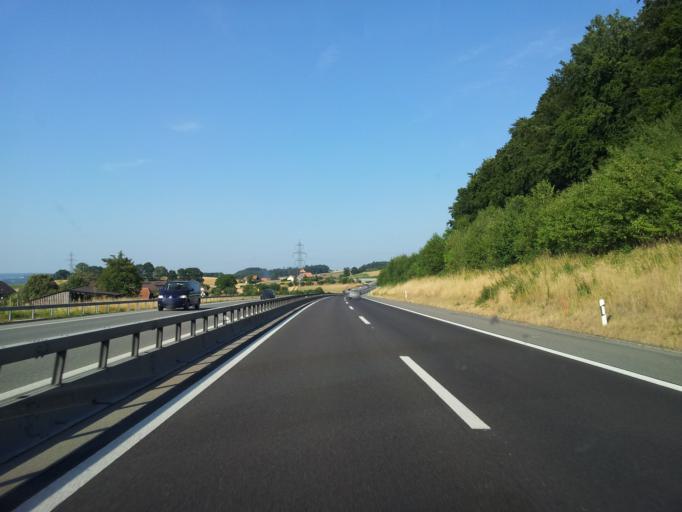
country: CH
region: Fribourg
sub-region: Sense District
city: Dudingen
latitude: 46.8646
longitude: 7.2082
